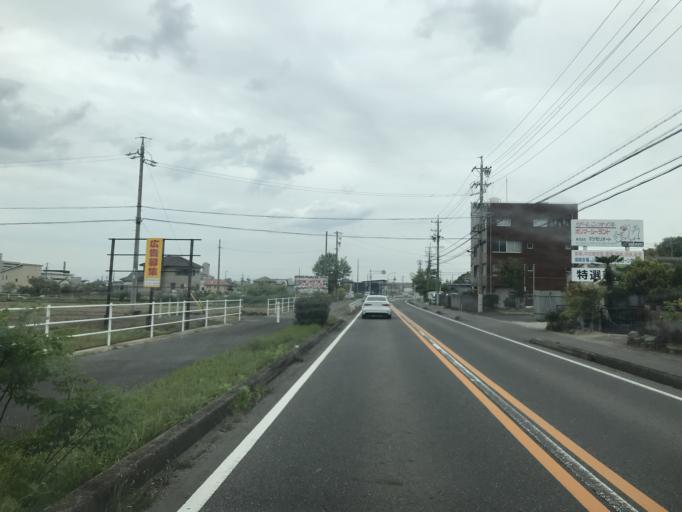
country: JP
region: Aichi
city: Kasugai
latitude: 35.2757
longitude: 136.9769
